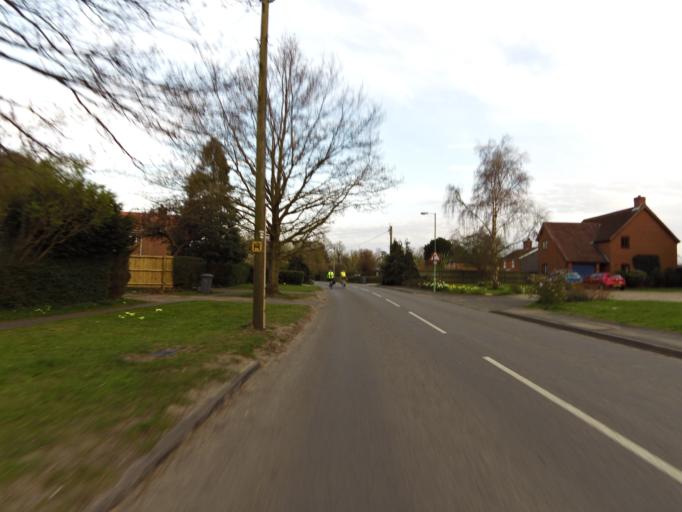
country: GB
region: England
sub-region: Suffolk
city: Debenham
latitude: 52.1509
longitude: 1.2204
